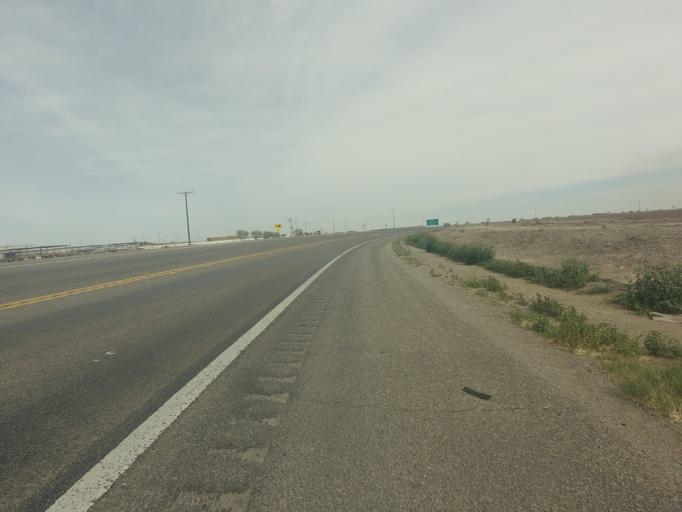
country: US
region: California
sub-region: Imperial County
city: Brawley
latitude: 32.9744
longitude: -115.4095
